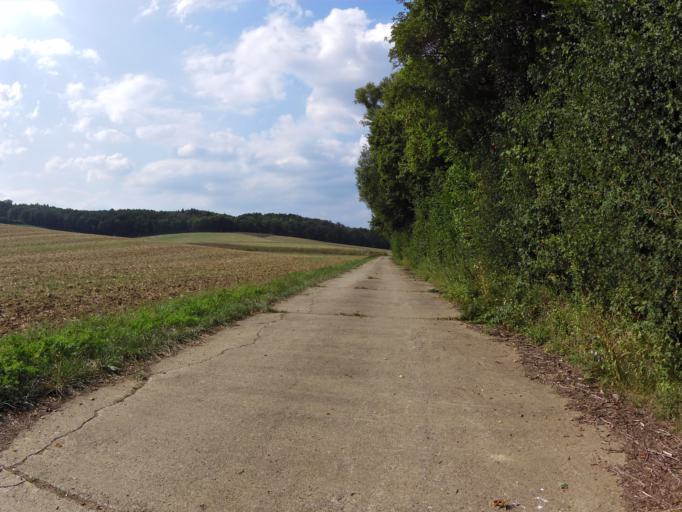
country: DE
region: Bavaria
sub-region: Regierungsbezirk Unterfranken
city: Kleinrinderfeld
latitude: 49.7079
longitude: 9.8345
